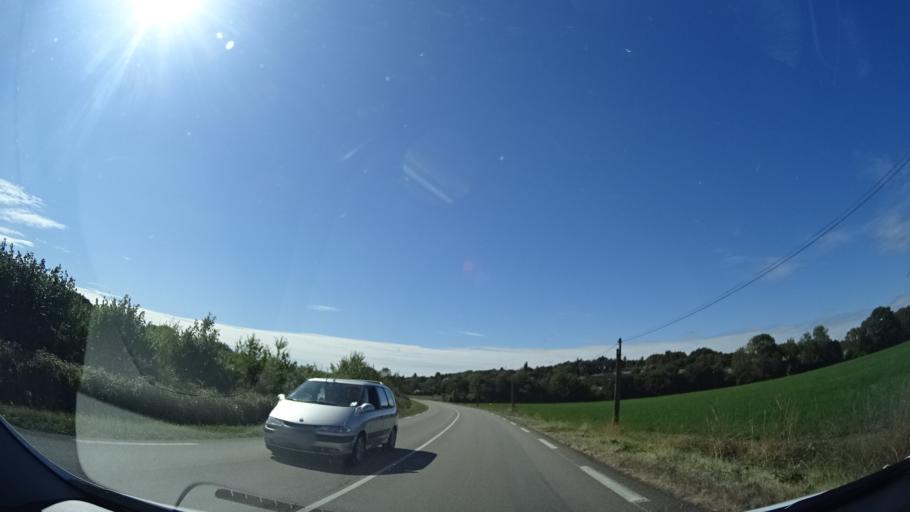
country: FR
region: Centre
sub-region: Departement du Loiret
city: Douchy
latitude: 47.9348
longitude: 3.0932
